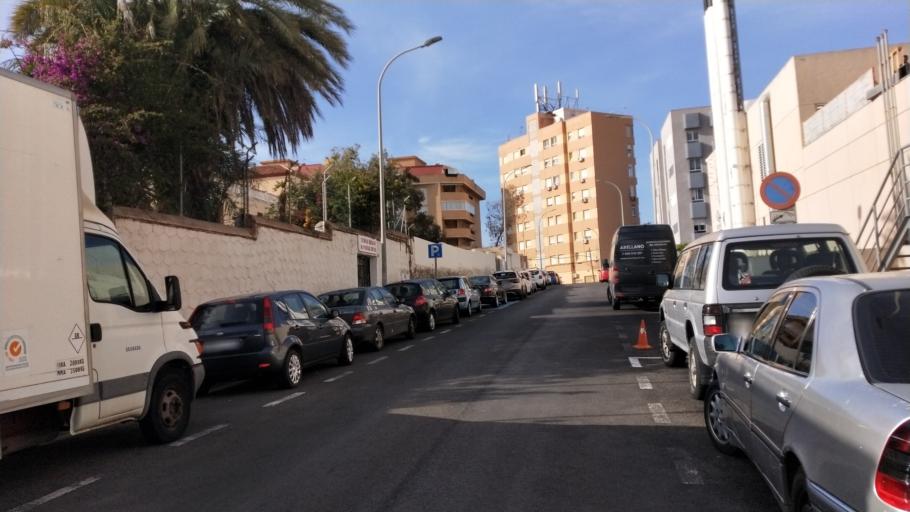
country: ES
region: Melilla
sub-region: Melilla
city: Melilla
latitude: 35.2863
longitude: -2.9482
